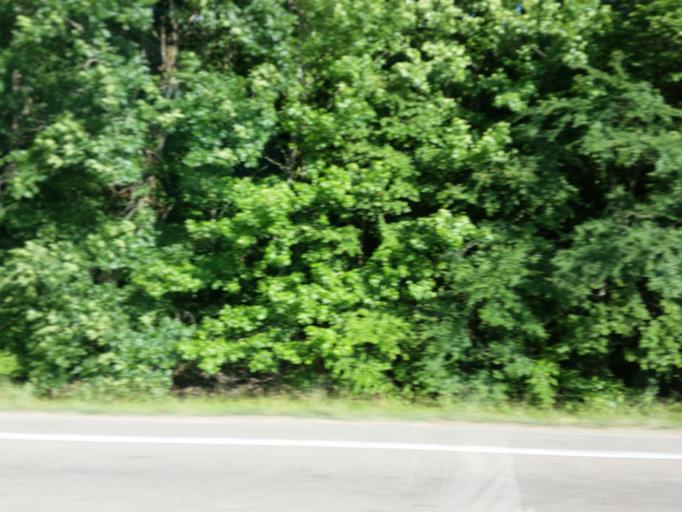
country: US
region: Mississippi
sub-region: Calhoun County
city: Calhoun City
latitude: 33.8234
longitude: -89.3391
